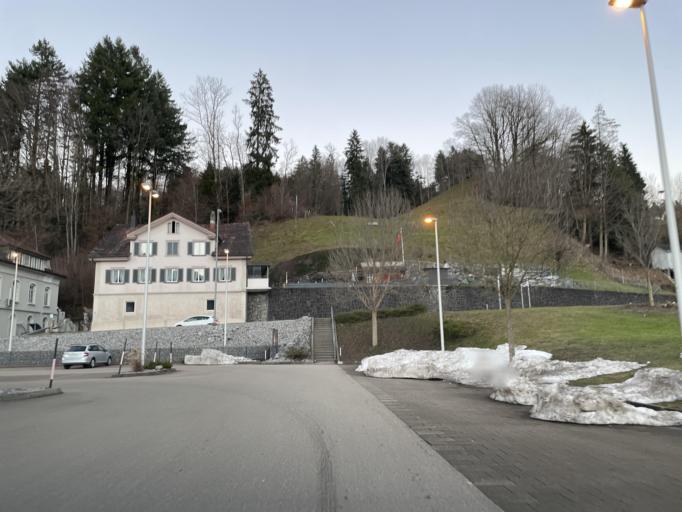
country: CH
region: Saint Gallen
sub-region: Wahlkreis Toggenburg
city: Wattwil
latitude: 47.2958
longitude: 9.0930
